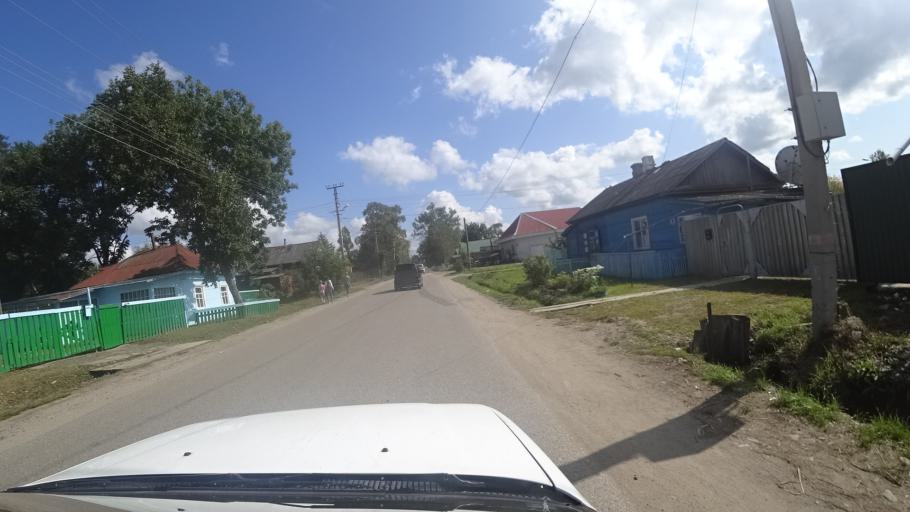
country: RU
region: Primorskiy
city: Dal'nerechensk
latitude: 45.9286
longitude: 133.7306
